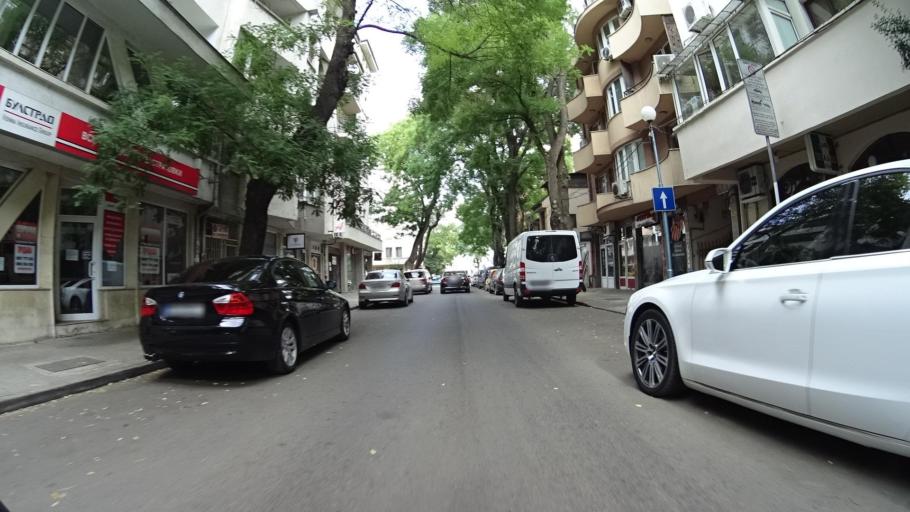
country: BG
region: Plovdiv
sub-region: Obshtina Plovdiv
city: Plovdiv
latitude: 42.1565
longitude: 24.7474
